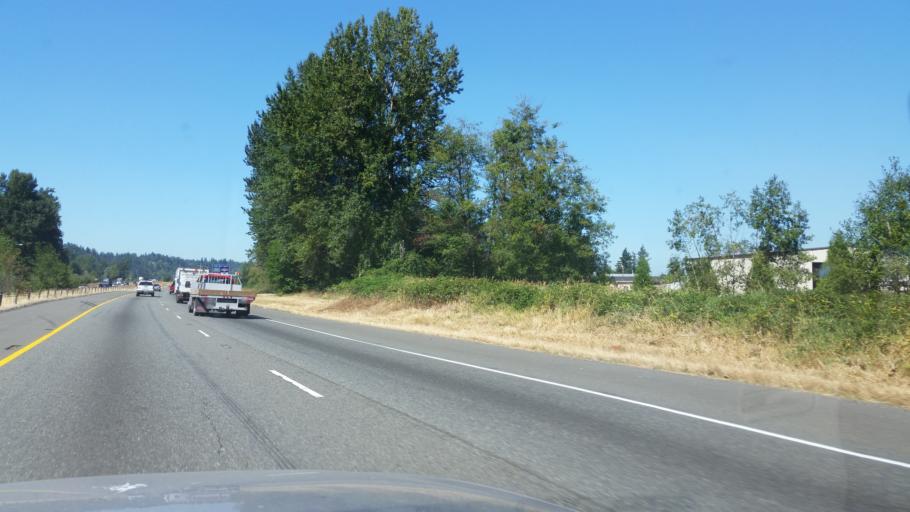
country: US
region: Washington
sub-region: King County
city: Pacific
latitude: 47.2427
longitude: -122.2548
